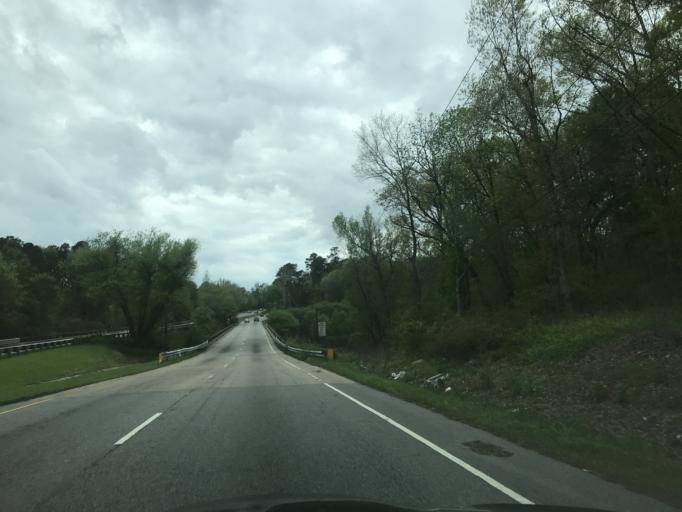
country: US
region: North Carolina
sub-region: Wake County
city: Knightdale
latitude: 35.7942
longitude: -78.5380
